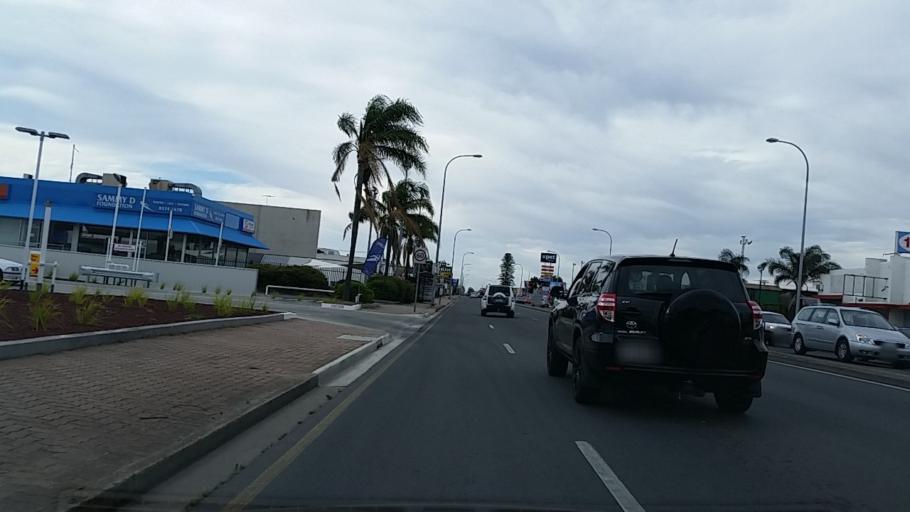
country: AU
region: South Australia
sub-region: Marion
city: Clovelly Park
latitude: -34.9926
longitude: 138.5748
